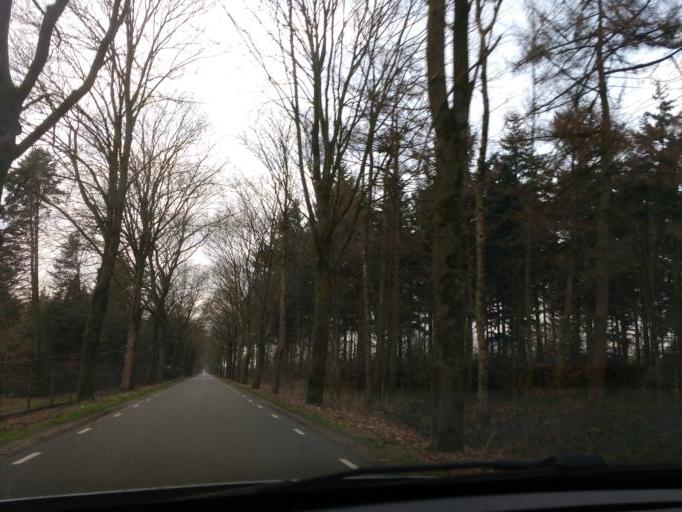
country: NL
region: North Brabant
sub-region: Gemeente Boxmeer
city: Overloon
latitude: 51.5749
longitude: 5.9813
